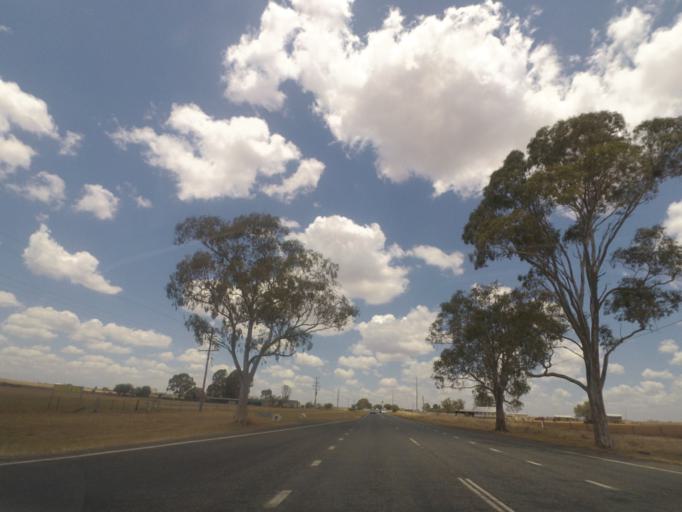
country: AU
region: Queensland
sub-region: Southern Downs
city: Warwick
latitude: -27.9281
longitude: 151.9851
